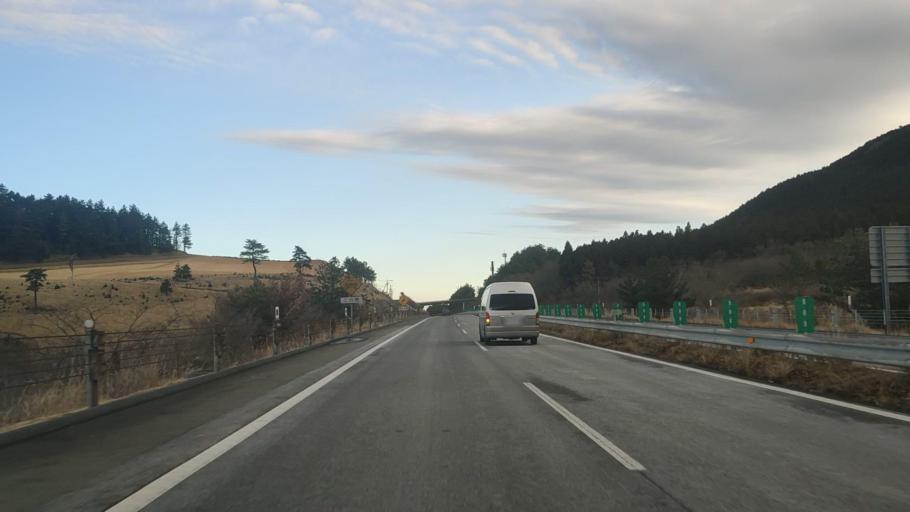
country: JP
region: Oita
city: Beppu
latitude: 33.3173
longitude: 131.4105
